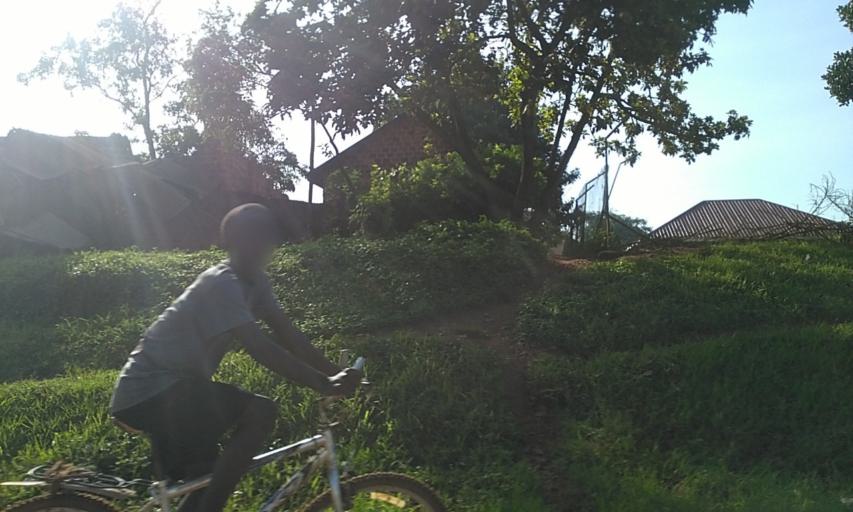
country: UG
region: Central Region
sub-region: Wakiso District
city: Kireka
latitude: 0.4427
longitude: 32.6080
